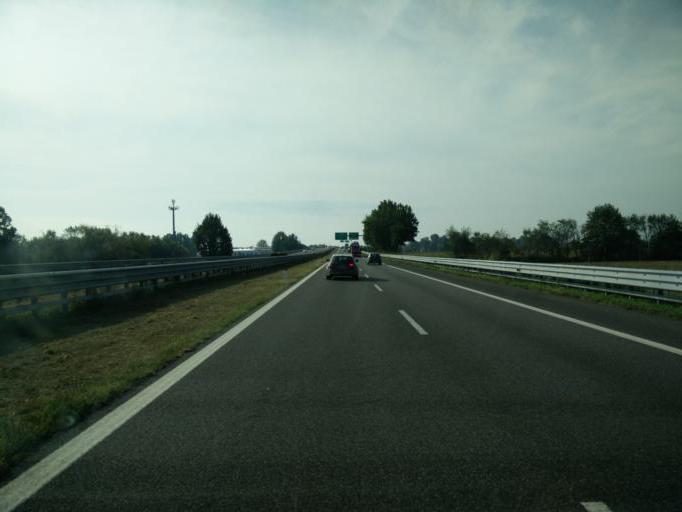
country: IT
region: Lombardy
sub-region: Provincia di Cremona
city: San Felice
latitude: 45.1516
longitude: 10.0742
